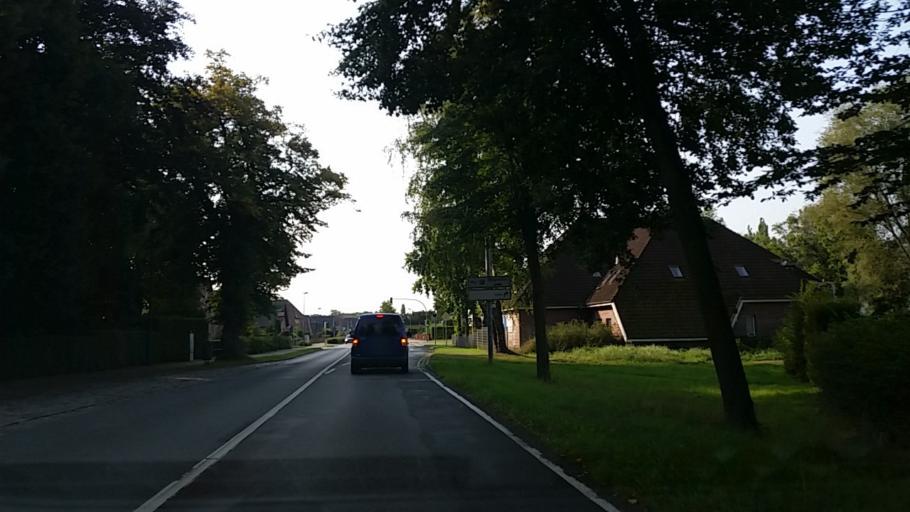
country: DE
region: Mecklenburg-Vorpommern
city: Hagenow
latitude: 53.4410
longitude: 11.1837
